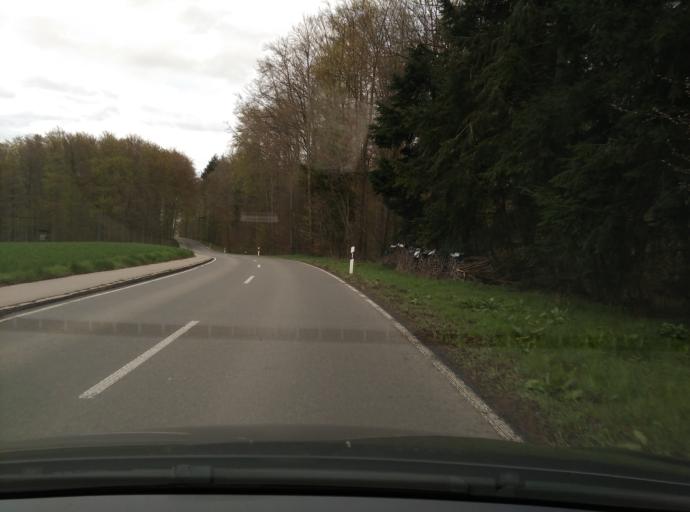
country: DE
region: Baden-Wuerttemberg
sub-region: Regierungsbezirk Stuttgart
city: Kohlberg
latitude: 48.5474
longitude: 9.3152
